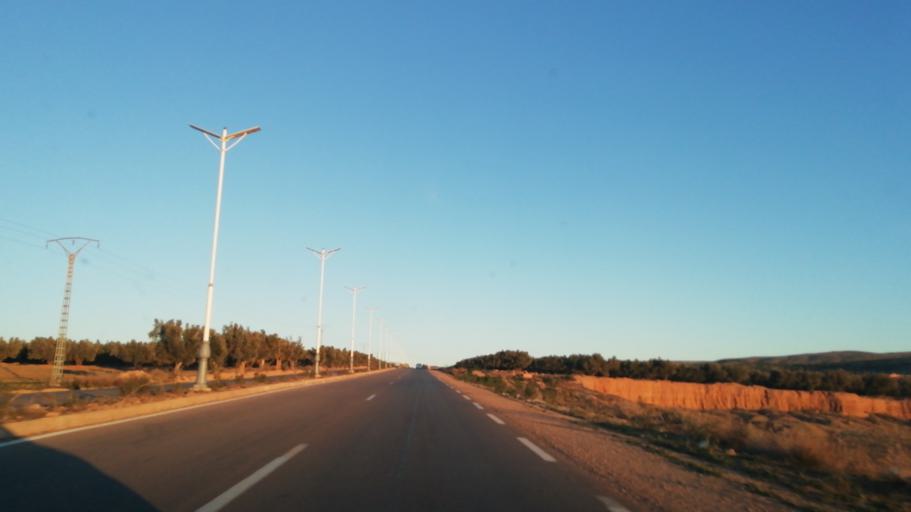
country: DZ
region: Saida
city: Saida
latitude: 34.8652
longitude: 0.1868
